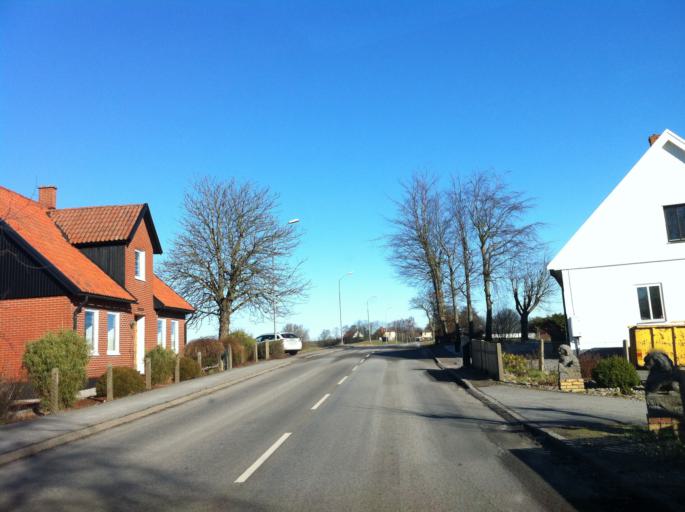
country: SE
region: Skane
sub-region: Svedala Kommun
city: Klagerup
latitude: 55.5737
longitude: 13.1979
